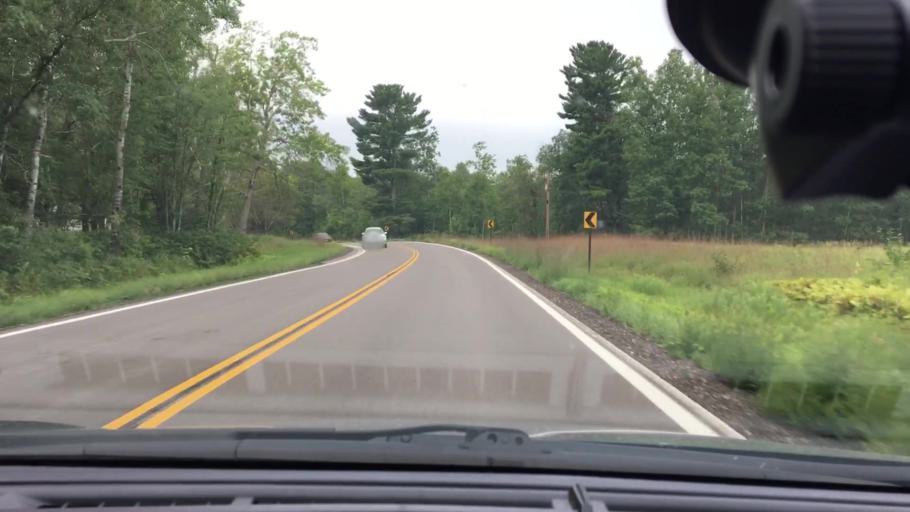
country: US
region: Minnesota
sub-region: Crow Wing County
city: Cross Lake
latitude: 46.6622
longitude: -93.9608
